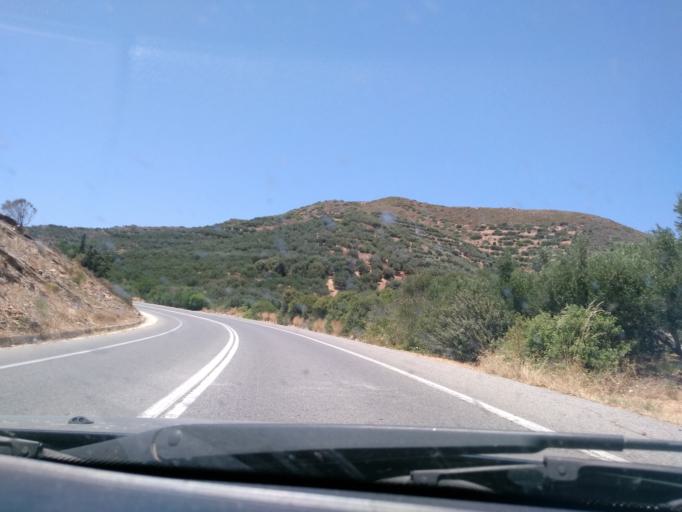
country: GR
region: Crete
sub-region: Nomos Rethymnis
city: Anogeia
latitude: 35.4024
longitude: 24.8672
